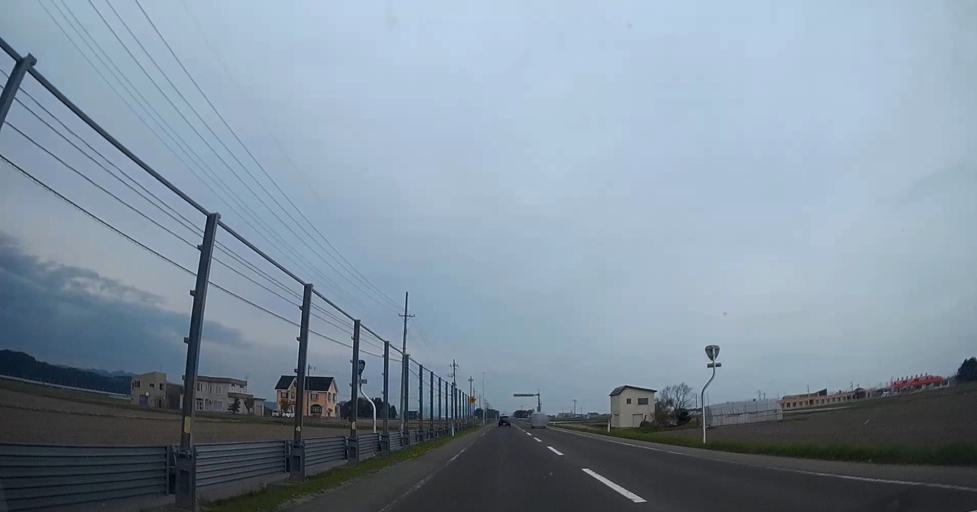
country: JP
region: Aomori
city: Aomori Shi
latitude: 40.8868
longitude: 140.6698
